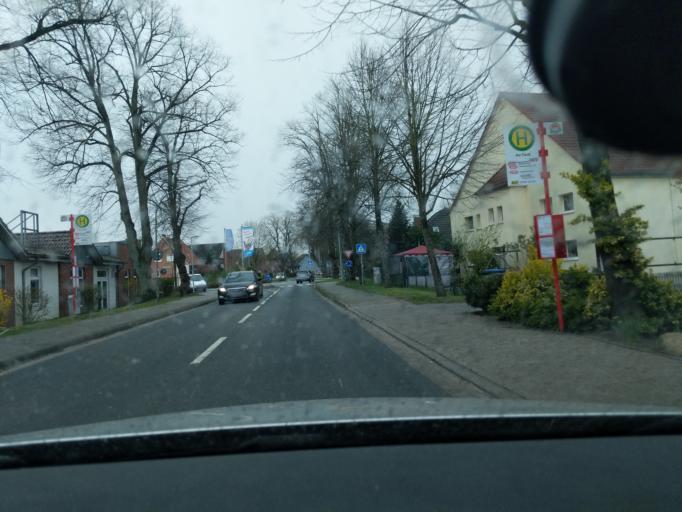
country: DE
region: Lower Saxony
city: Horneburg
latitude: 53.5041
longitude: 9.5888
